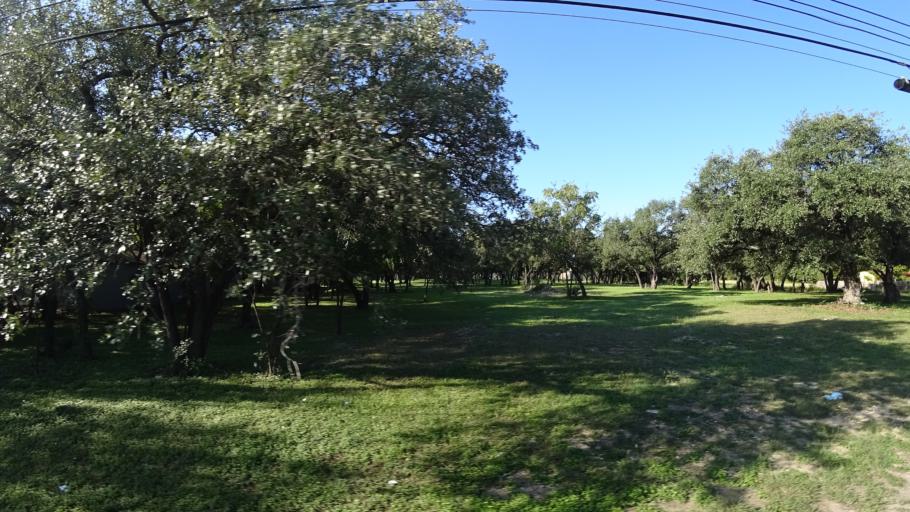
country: US
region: Texas
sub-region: Travis County
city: Austin
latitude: 30.3458
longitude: -97.6996
